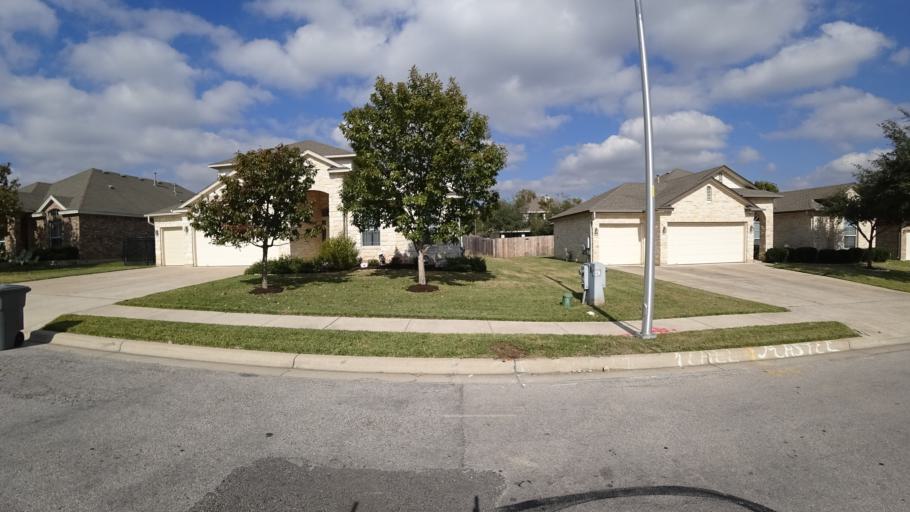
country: US
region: Texas
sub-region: Travis County
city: Shady Hollow
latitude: 30.1613
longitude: -97.8491
